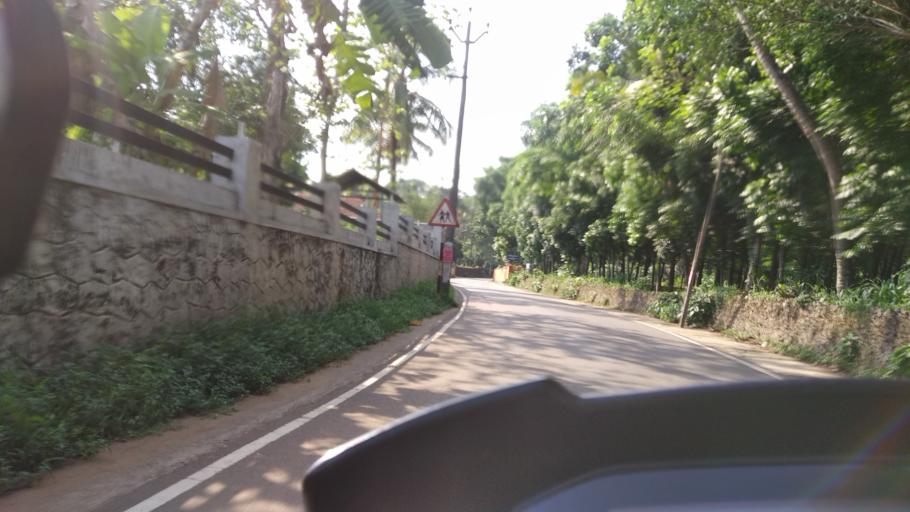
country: IN
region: Kerala
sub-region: Ernakulam
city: Piravam
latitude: 9.8324
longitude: 76.5436
